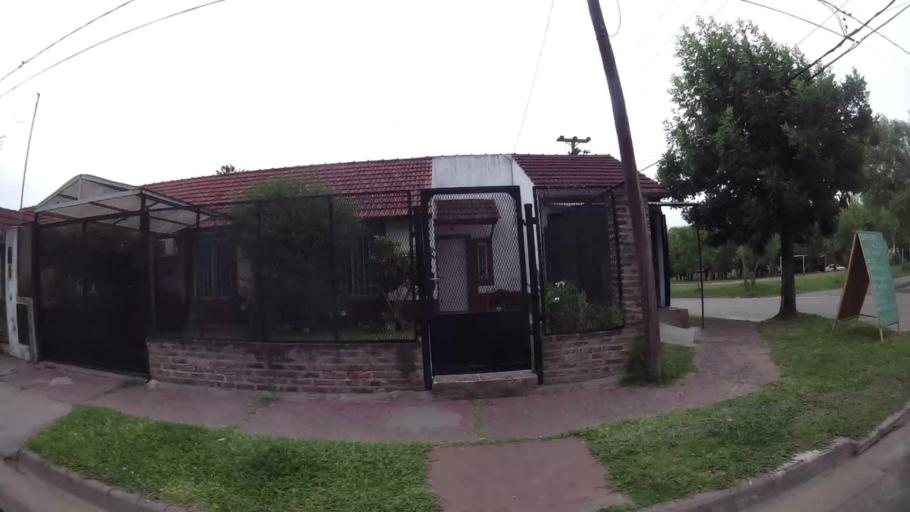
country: AR
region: Buenos Aires
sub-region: Partido de Campana
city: Campana
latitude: -34.2103
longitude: -58.9442
